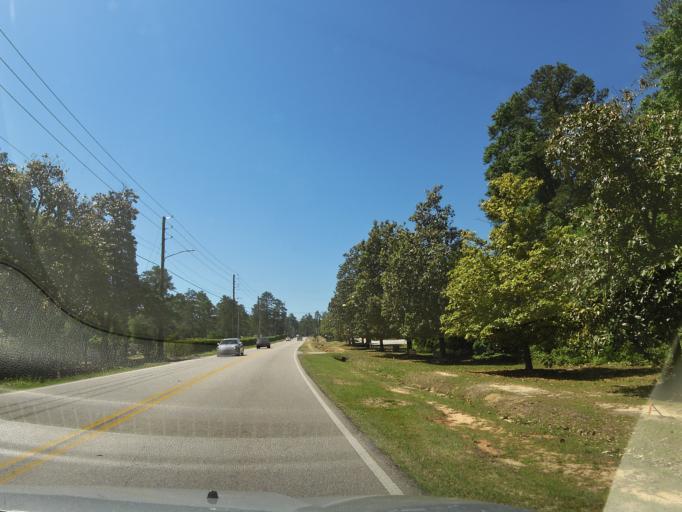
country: US
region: Georgia
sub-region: Columbia County
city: Martinez
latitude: 33.4887
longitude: -82.0292
